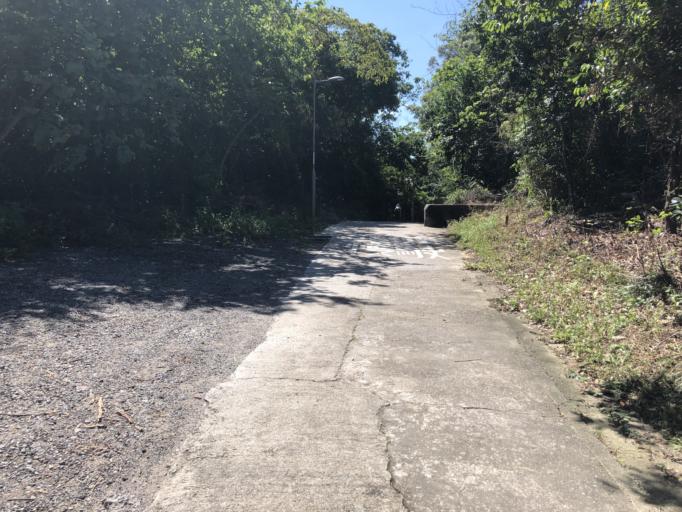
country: HK
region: Tuen Mun
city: Tuen Mun
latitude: 22.2938
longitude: 113.9741
